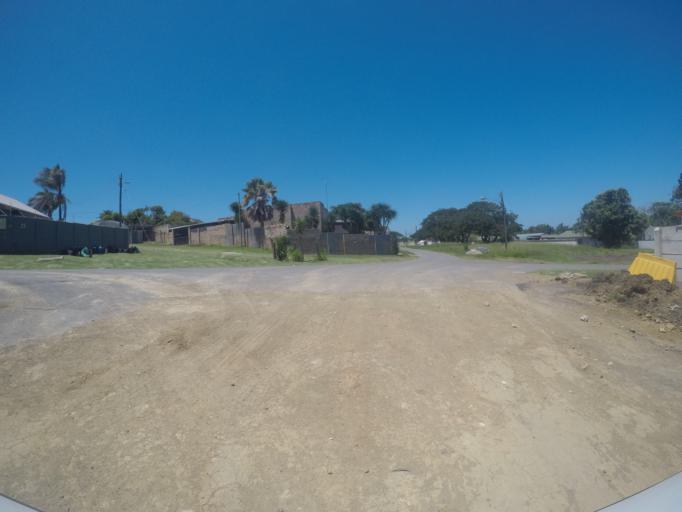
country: ZA
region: Eastern Cape
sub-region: Buffalo City Metropolitan Municipality
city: East London
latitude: -32.9559
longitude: 27.9959
